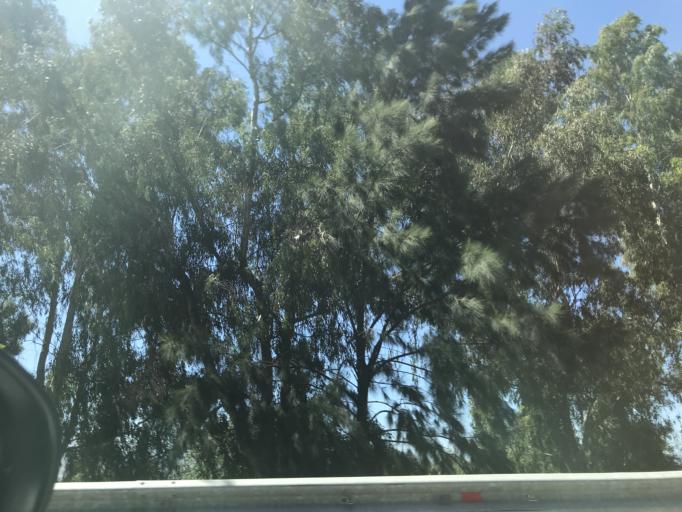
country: TR
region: Aydin
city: Aydin
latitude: 37.8173
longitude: 27.8451
